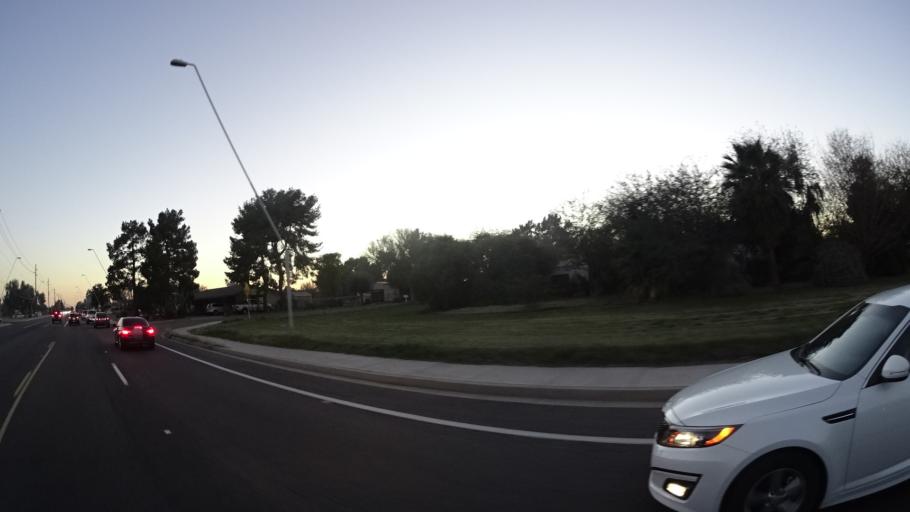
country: US
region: Arizona
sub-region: Maricopa County
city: San Carlos
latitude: 33.3446
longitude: -111.8765
